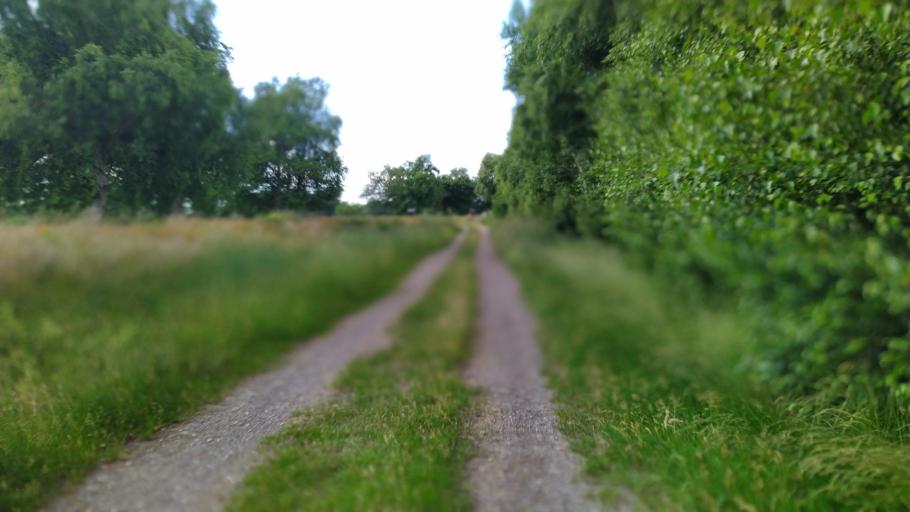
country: DE
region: Lower Saxony
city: Stinstedt
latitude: 53.6491
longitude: 8.9465
